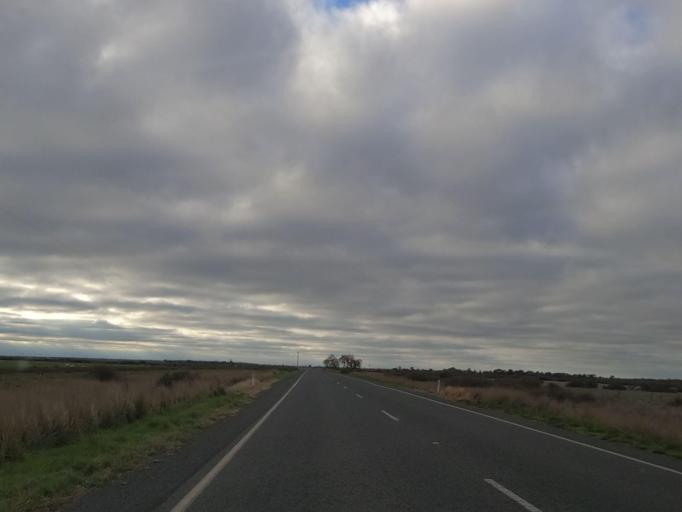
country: AU
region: Victoria
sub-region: Swan Hill
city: Swan Hill
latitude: -35.8523
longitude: 143.9368
